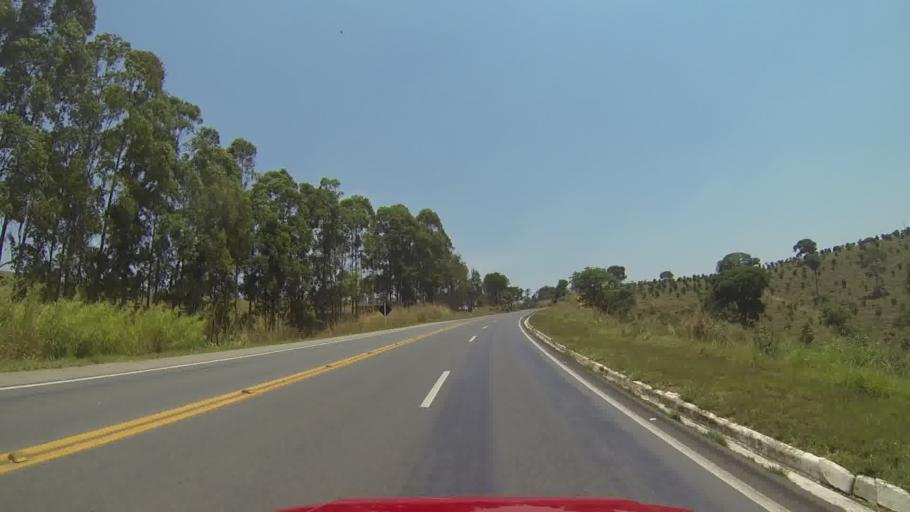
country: BR
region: Minas Gerais
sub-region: Itapecerica
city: Itapecerica
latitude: -20.3406
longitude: -45.2384
